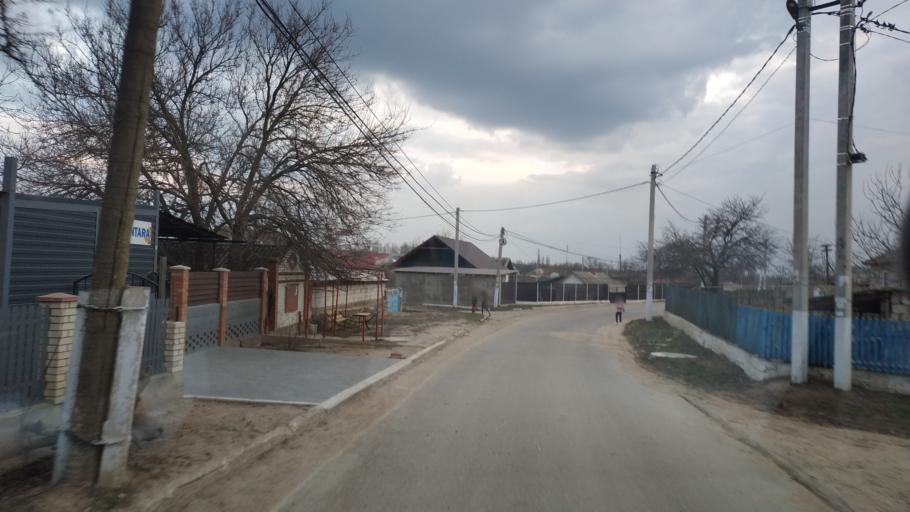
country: MD
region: Telenesti
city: Grigoriopol
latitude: 47.0231
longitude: 29.3587
